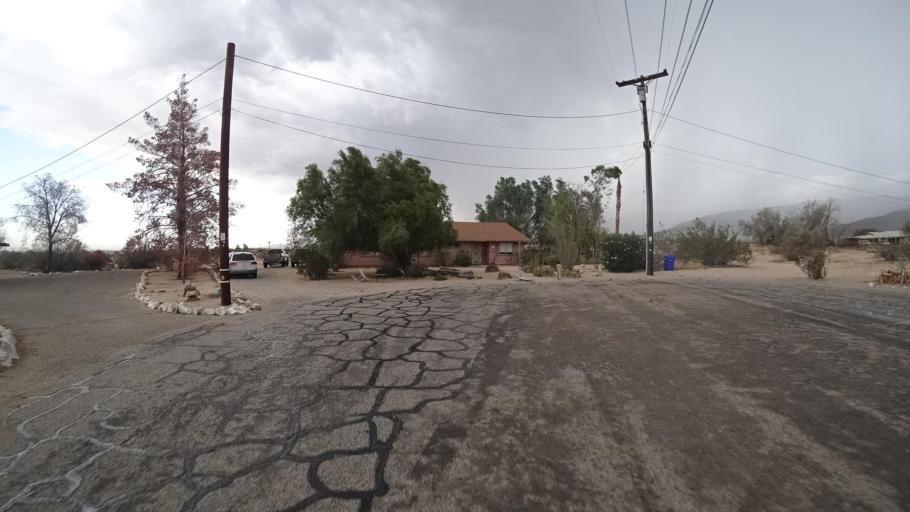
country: US
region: California
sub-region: San Diego County
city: Borrego Springs
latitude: 33.2820
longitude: -116.3918
